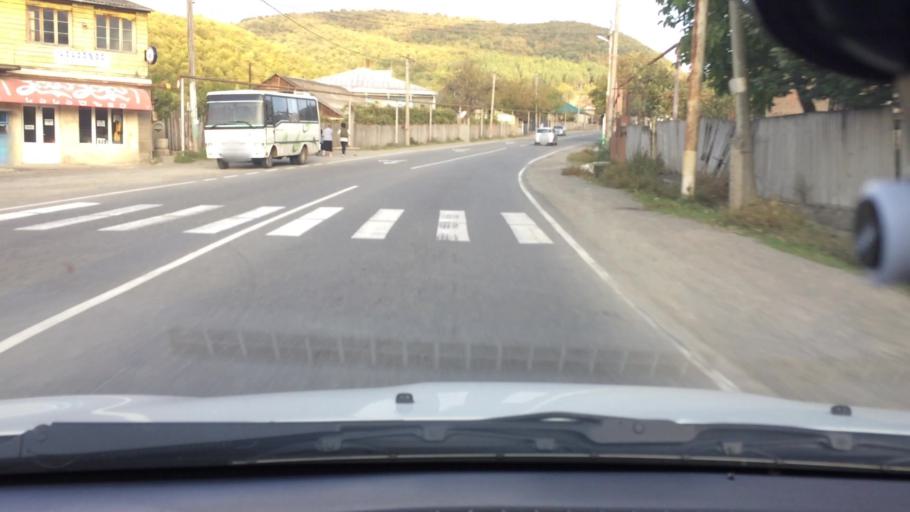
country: GE
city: Surami
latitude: 42.0306
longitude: 43.5256
